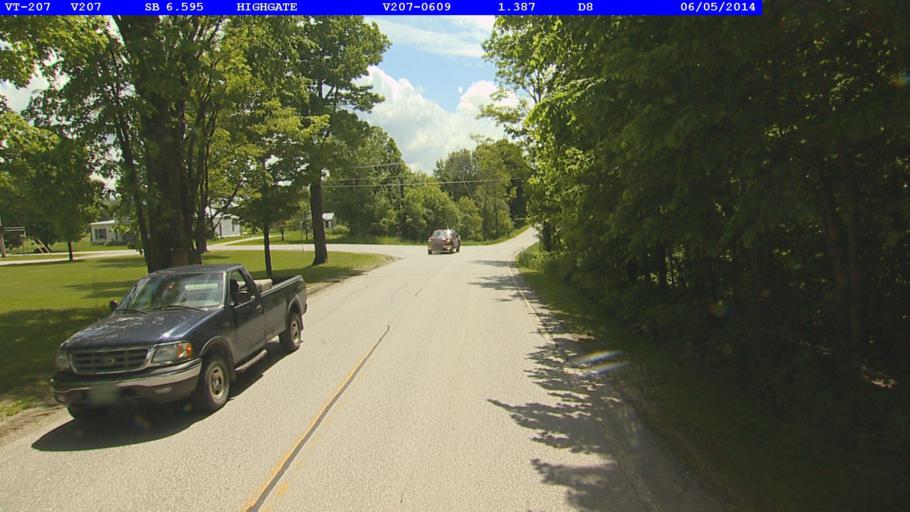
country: US
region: Vermont
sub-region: Franklin County
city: Swanton
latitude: 44.9304
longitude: -73.0490
